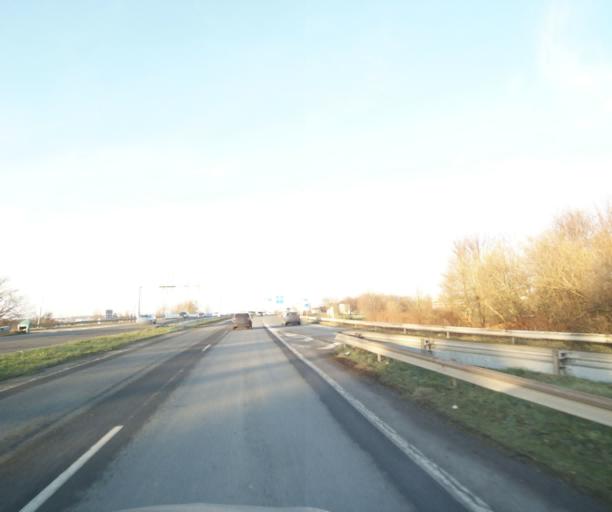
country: FR
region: Nord-Pas-de-Calais
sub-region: Departement du Nord
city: Famars
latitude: 50.3361
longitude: 3.5131
